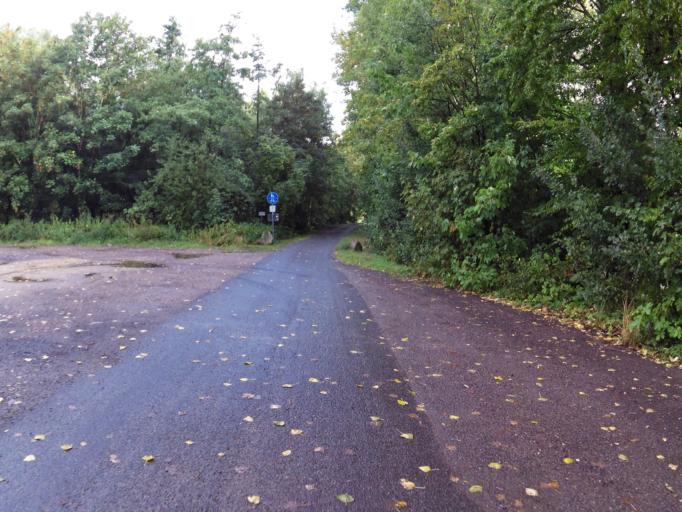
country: DE
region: Lower Saxony
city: Nienburg
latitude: 52.6457
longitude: 9.2037
